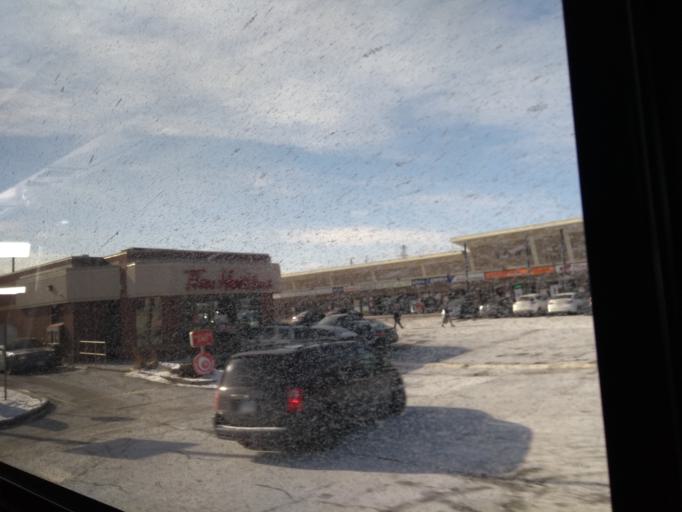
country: CA
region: Ontario
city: Niagara Falls
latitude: 43.0982
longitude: -79.0857
